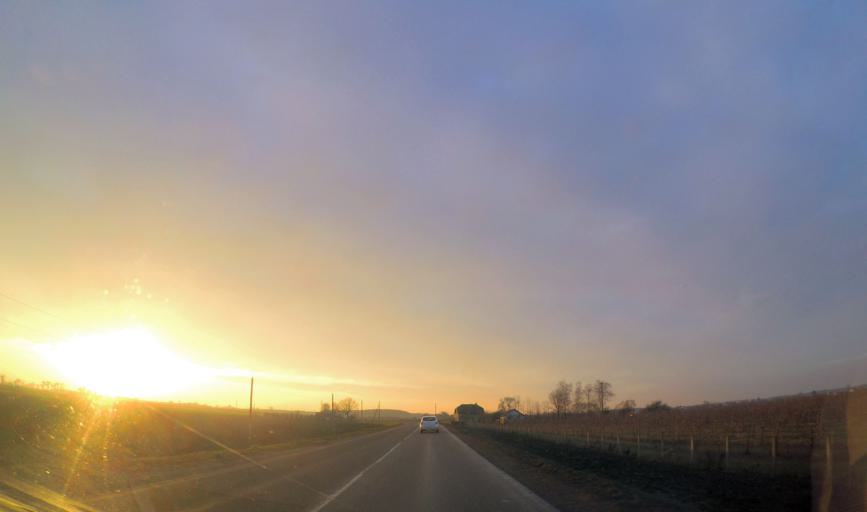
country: BY
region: Grodnenskaya
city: Hrodna
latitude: 53.7339
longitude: 23.9192
